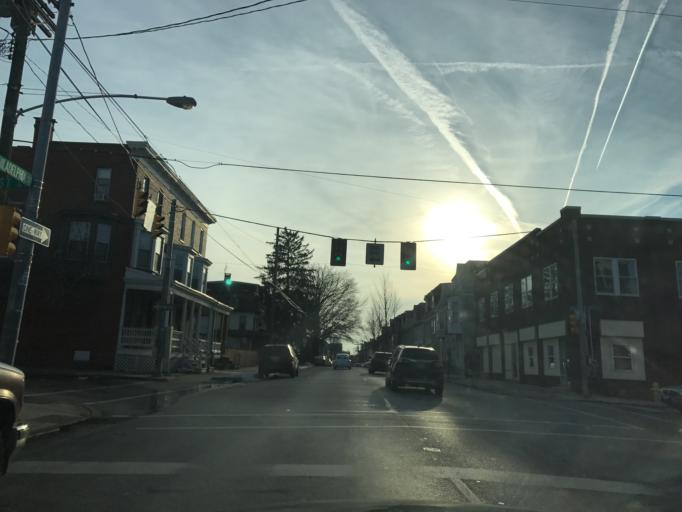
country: US
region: Pennsylvania
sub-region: York County
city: West York
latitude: 39.9591
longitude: -76.7437
